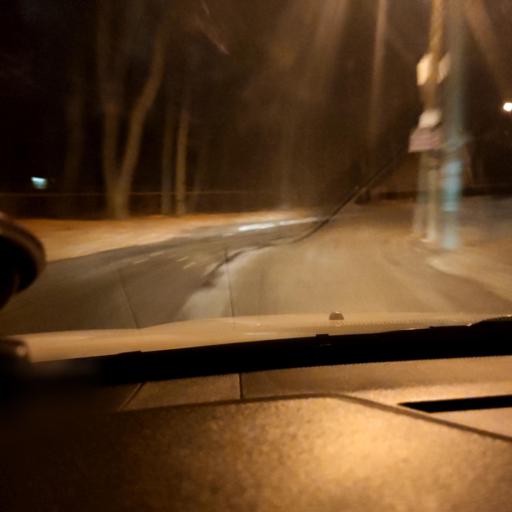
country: RU
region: Samara
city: Samara
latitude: 53.2884
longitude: 50.1985
